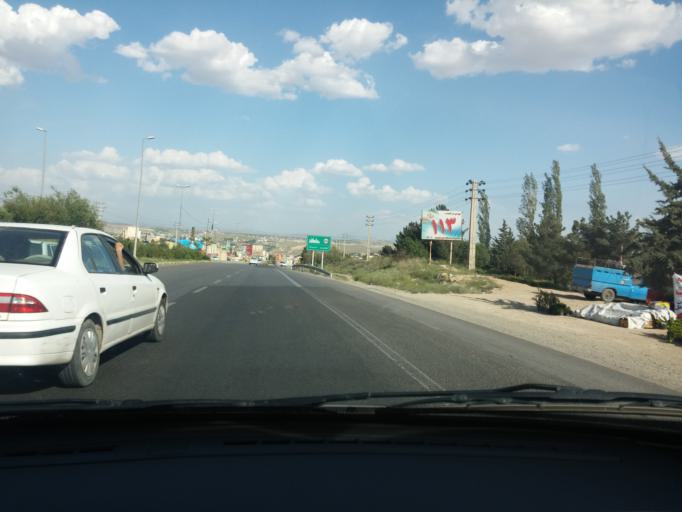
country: IR
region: Tehran
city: Damavand
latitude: 35.6923
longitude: 52.0056
